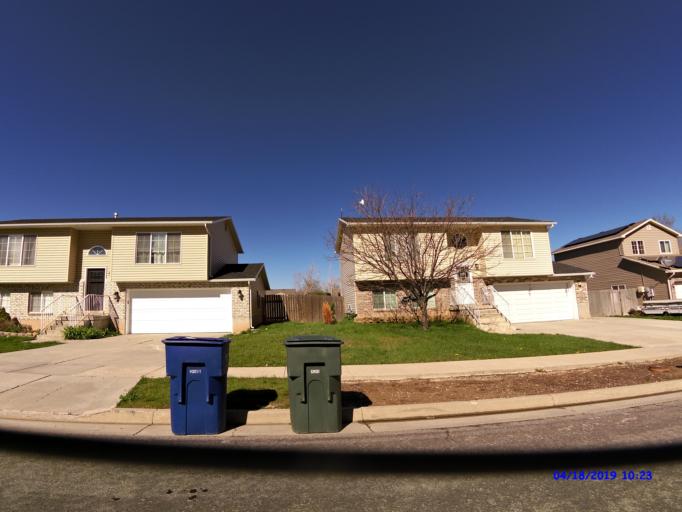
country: US
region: Utah
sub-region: Weber County
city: Harrisville
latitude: 41.2695
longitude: -111.9641
